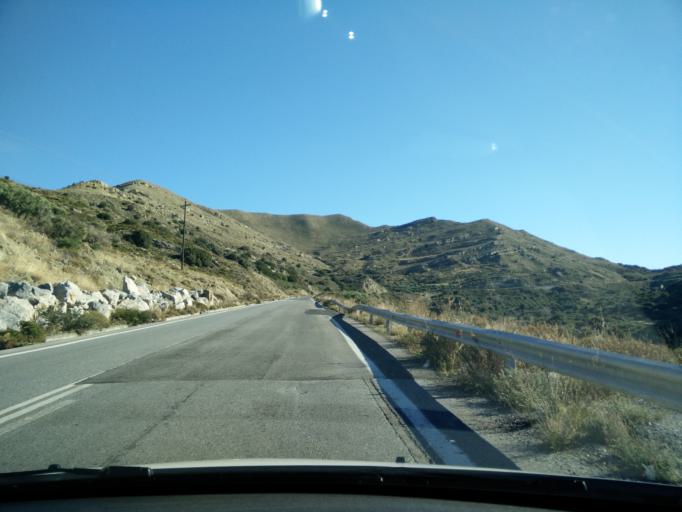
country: GR
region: Crete
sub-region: Nomos Irakleiou
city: Arkalochori
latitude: 35.0647
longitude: 25.3568
